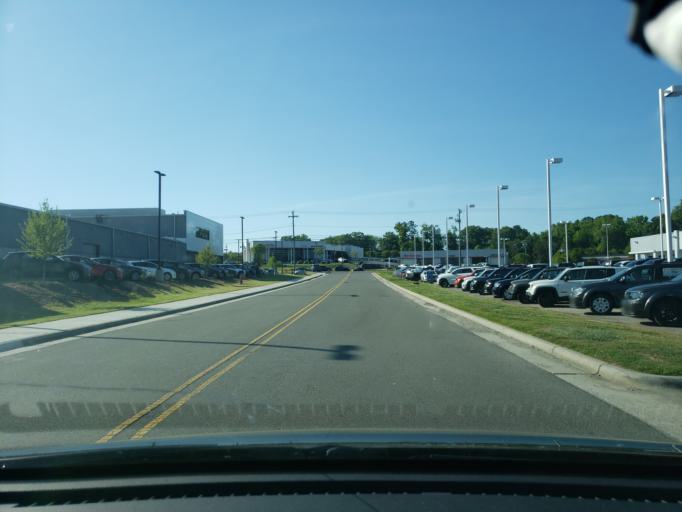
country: US
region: North Carolina
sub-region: Durham County
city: Durham
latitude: 35.9614
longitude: -78.9740
